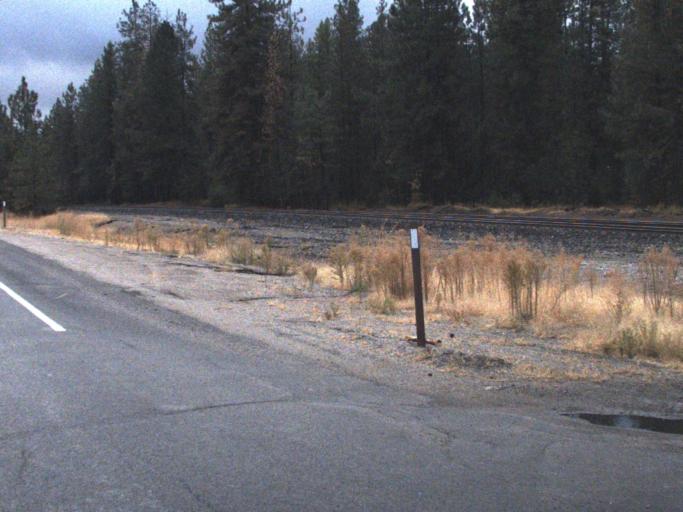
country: US
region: Washington
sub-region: Spokane County
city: Deer Park
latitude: 48.0616
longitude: -117.6331
